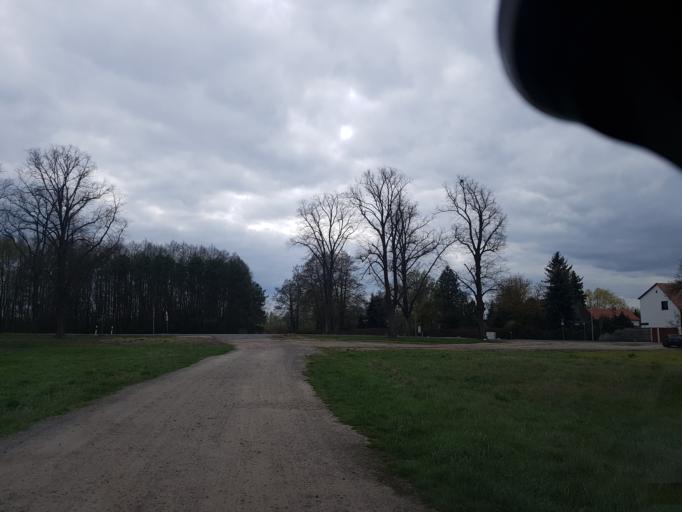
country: DE
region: Brandenburg
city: Bruck
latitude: 52.1999
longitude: 12.7770
